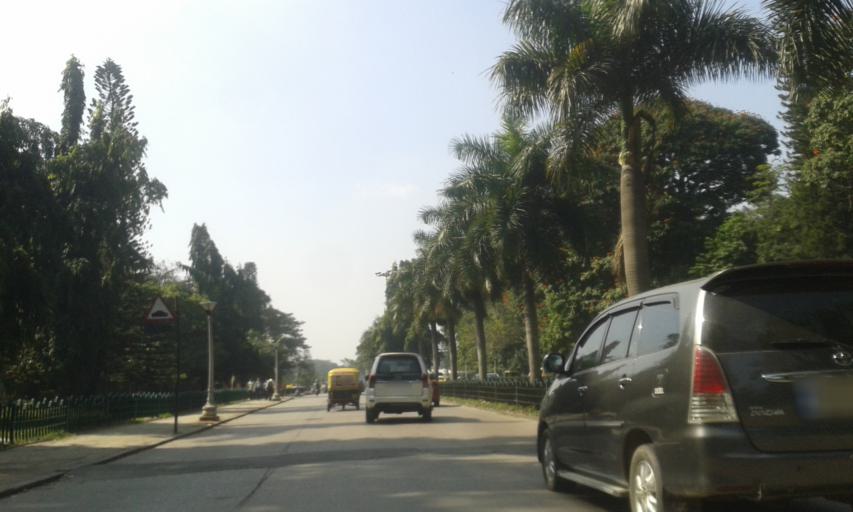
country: IN
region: Karnataka
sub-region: Bangalore Urban
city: Bangalore
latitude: 12.9815
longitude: 77.5945
